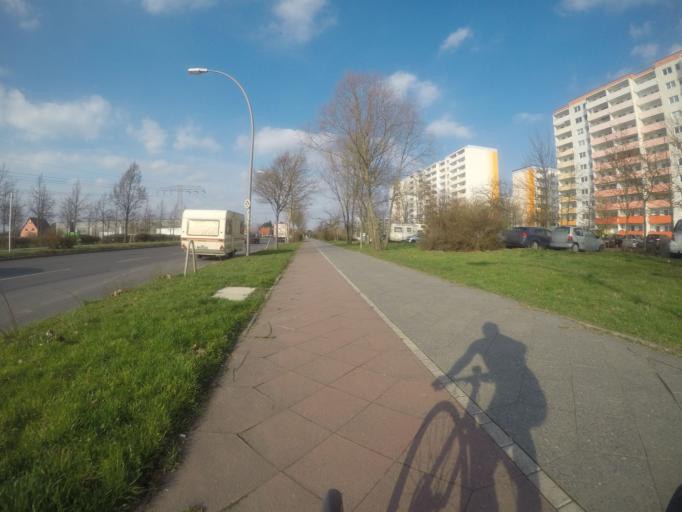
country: DE
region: Berlin
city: Altglienicke
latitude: 52.4047
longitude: 13.5237
